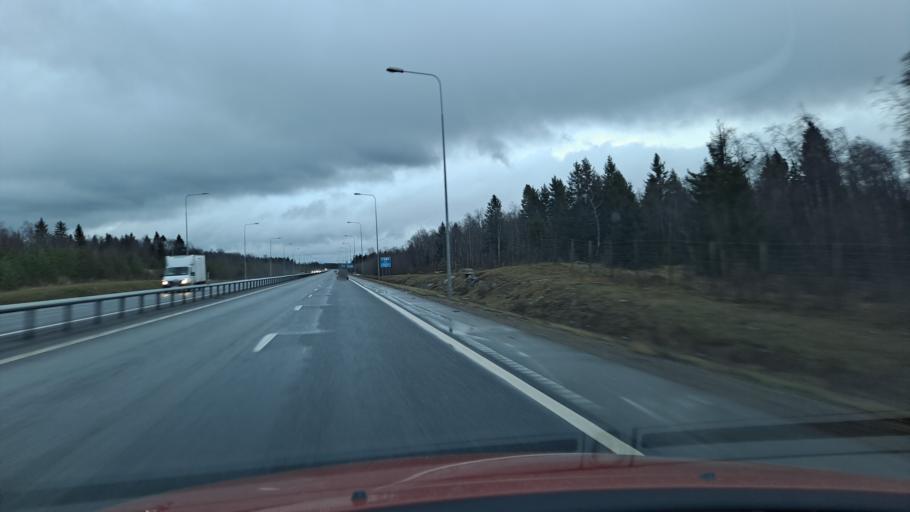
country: FI
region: Lapland
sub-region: Kemi-Tornio
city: Kemi
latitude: 65.7081
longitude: 24.6364
